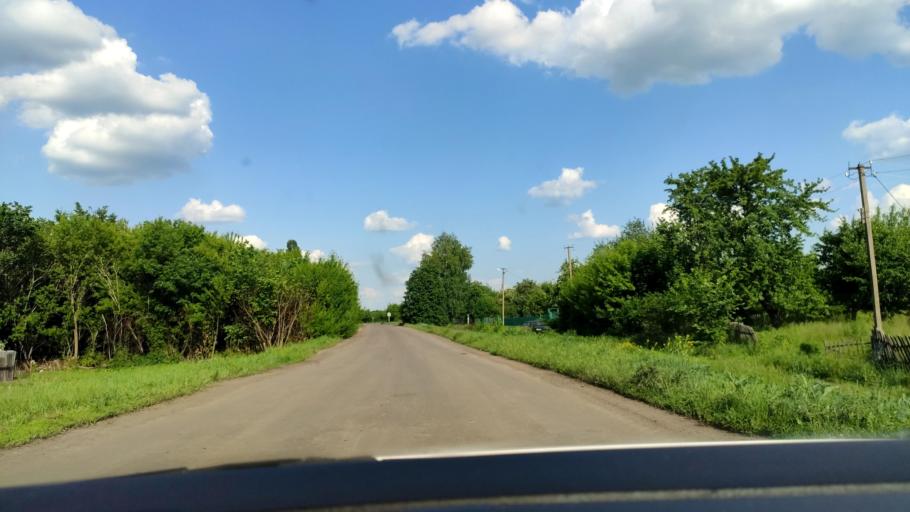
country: RU
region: Voronezj
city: Panino
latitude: 51.6102
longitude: 40.0554
